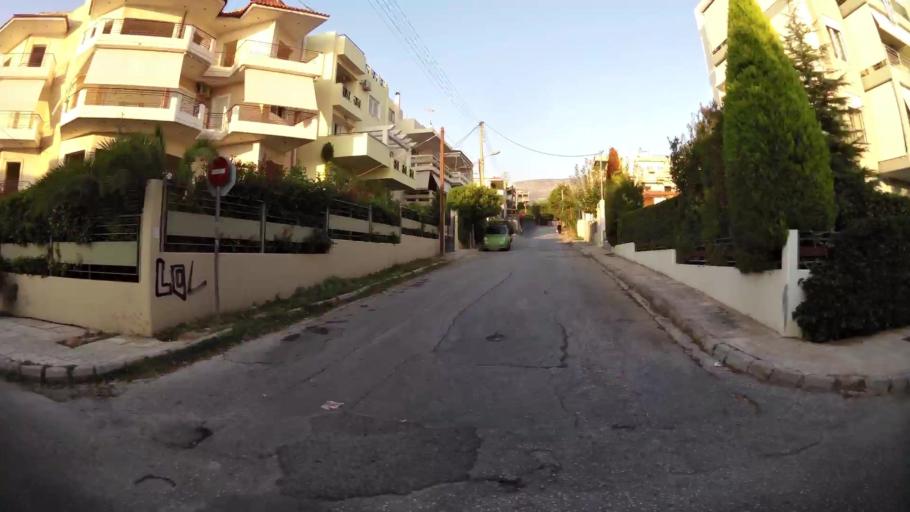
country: GR
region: Attica
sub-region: Nomarchia Athinas
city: Glyfada
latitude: 37.8834
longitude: 23.7709
